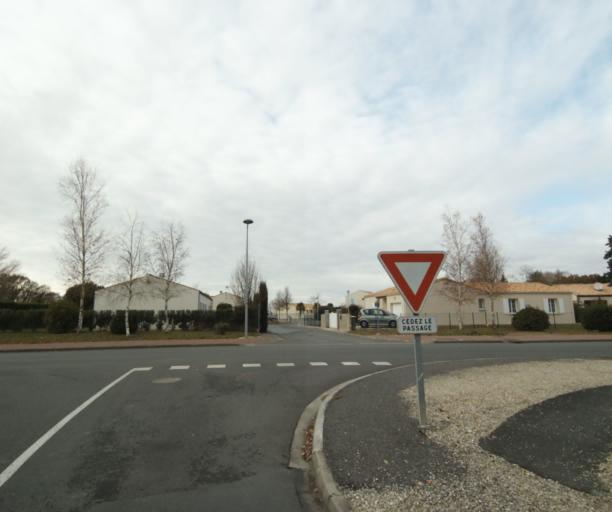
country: FR
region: Poitou-Charentes
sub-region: Departement de la Charente-Maritime
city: Corme-Royal
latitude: 45.7408
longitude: -0.8148
